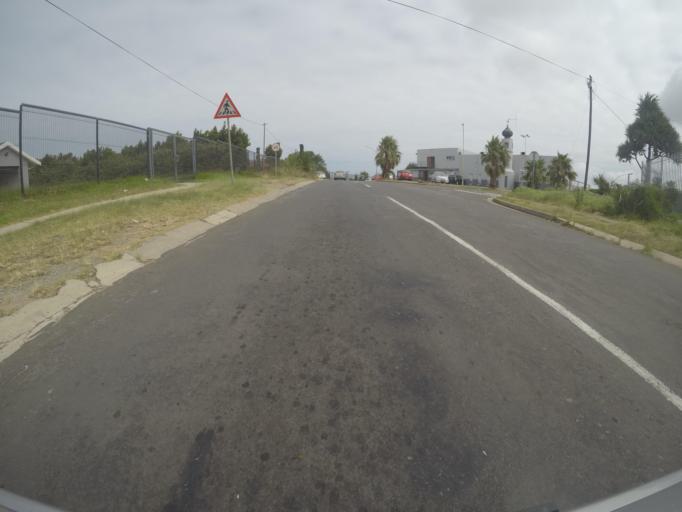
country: ZA
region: Eastern Cape
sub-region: Buffalo City Metropolitan Municipality
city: East London
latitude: -33.0020
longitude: 27.8856
